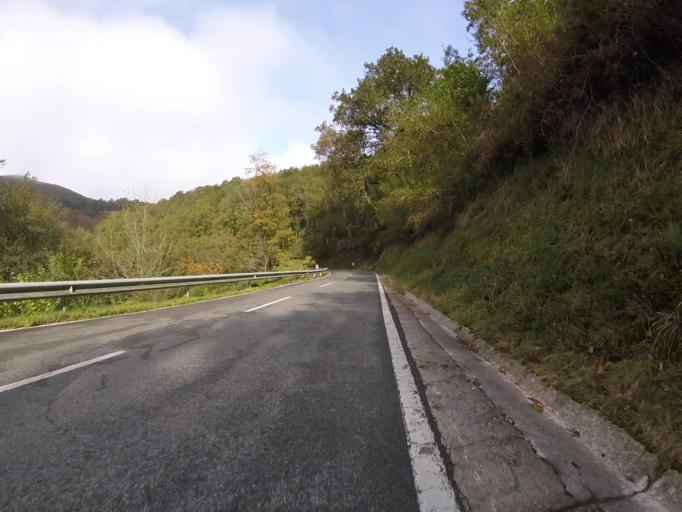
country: ES
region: Navarre
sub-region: Provincia de Navarra
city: Goizueta
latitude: 43.2011
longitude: -1.8572
